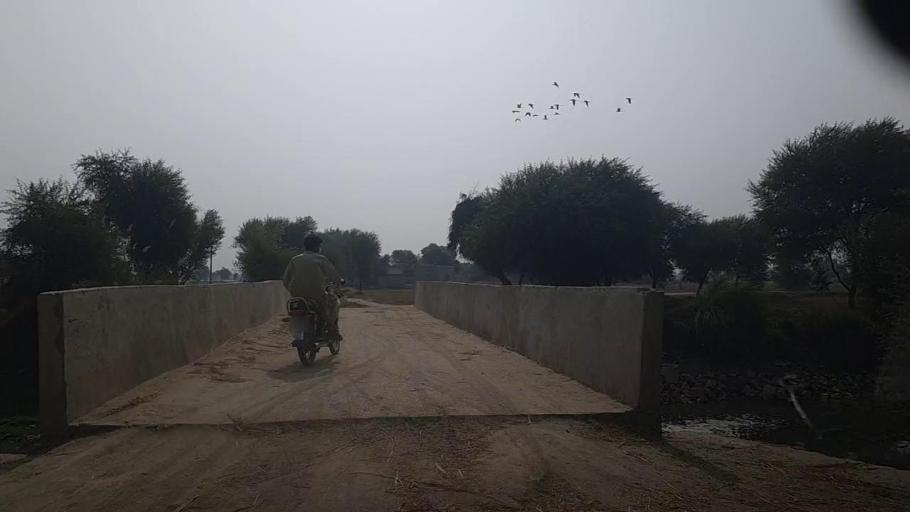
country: PK
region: Sindh
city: Kashmor
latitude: 28.4000
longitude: 69.4202
